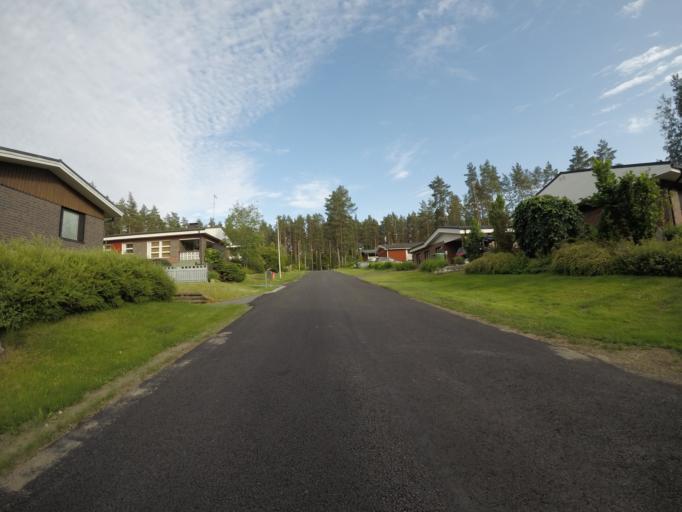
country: FI
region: Haeme
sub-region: Haemeenlinna
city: Haemeenlinna
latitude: 60.9723
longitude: 24.3959
